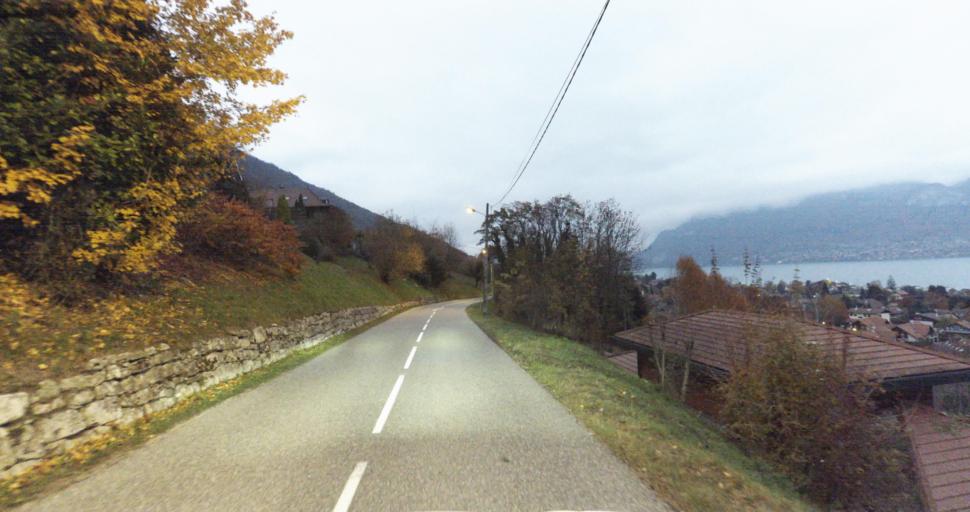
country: FR
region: Rhone-Alpes
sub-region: Departement de la Haute-Savoie
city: Sevrier
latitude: 45.8539
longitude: 6.1381
